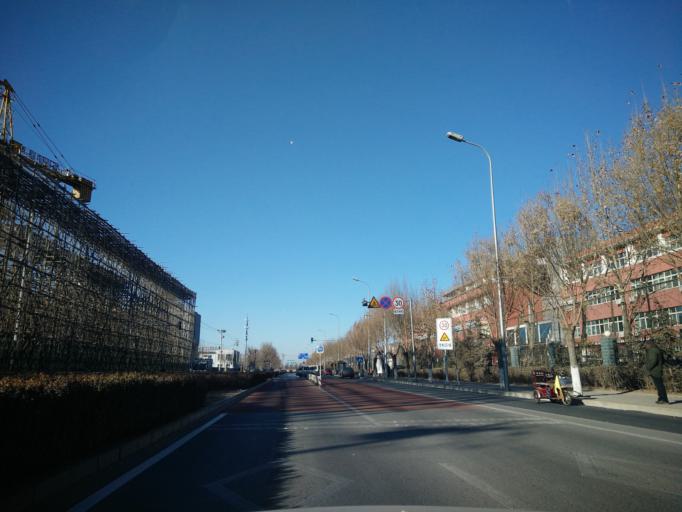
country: CN
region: Beijing
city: Yinghai
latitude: 39.7085
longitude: 116.3963
